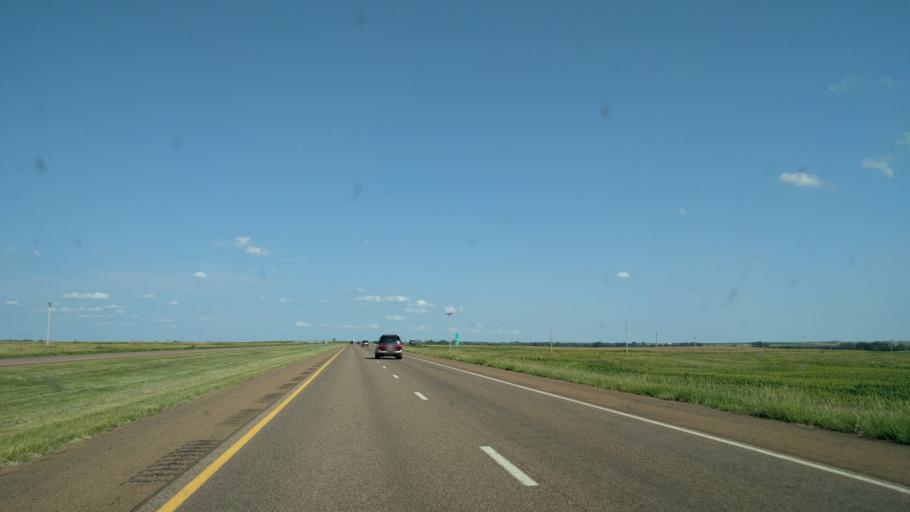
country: US
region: Kansas
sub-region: Ellis County
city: Ellis
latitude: 38.9542
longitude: -99.6084
